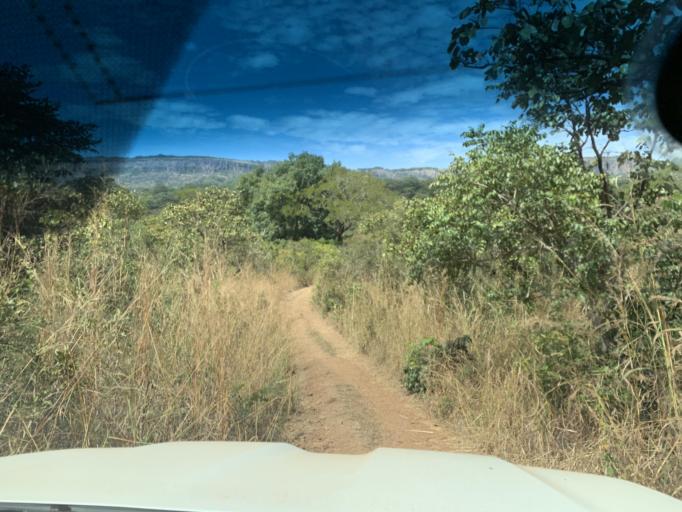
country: GN
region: Mamou
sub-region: Pita
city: Pita
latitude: 10.9958
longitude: -12.4898
